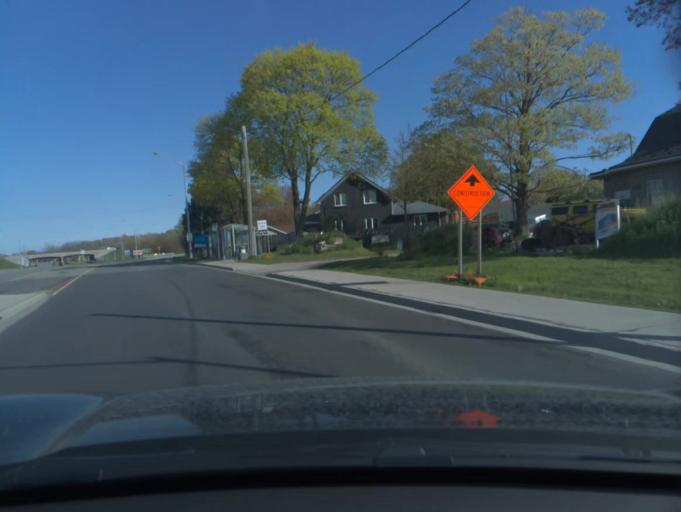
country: CA
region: Ontario
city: North Perth
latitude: 43.7992
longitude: -80.9998
